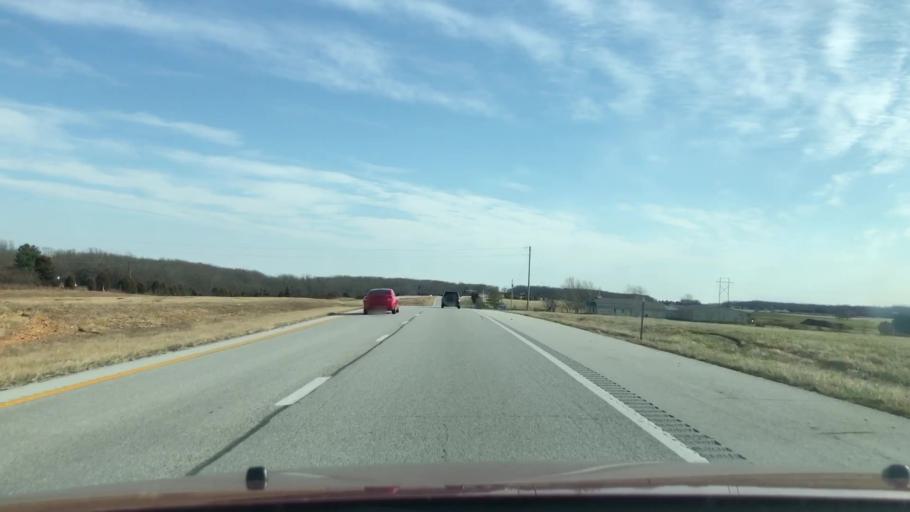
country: US
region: Missouri
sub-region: Webster County
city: Seymour
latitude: 37.1183
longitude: -92.6923
